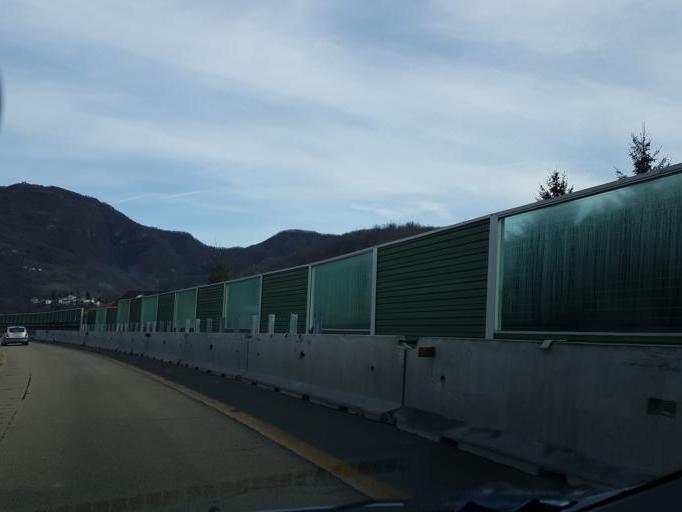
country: IT
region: Liguria
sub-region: Provincia di Genova
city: Ronco Scrivia
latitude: 44.6056
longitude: 8.9566
